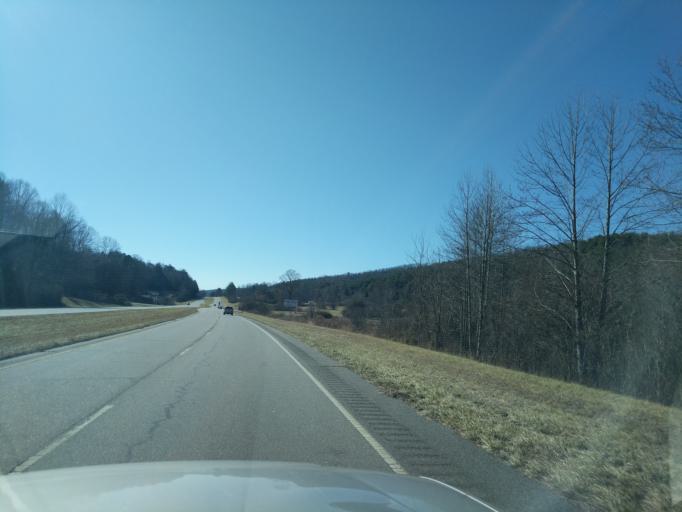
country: US
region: North Carolina
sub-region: Cherokee County
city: Murphy
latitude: 35.1566
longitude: -83.9545
